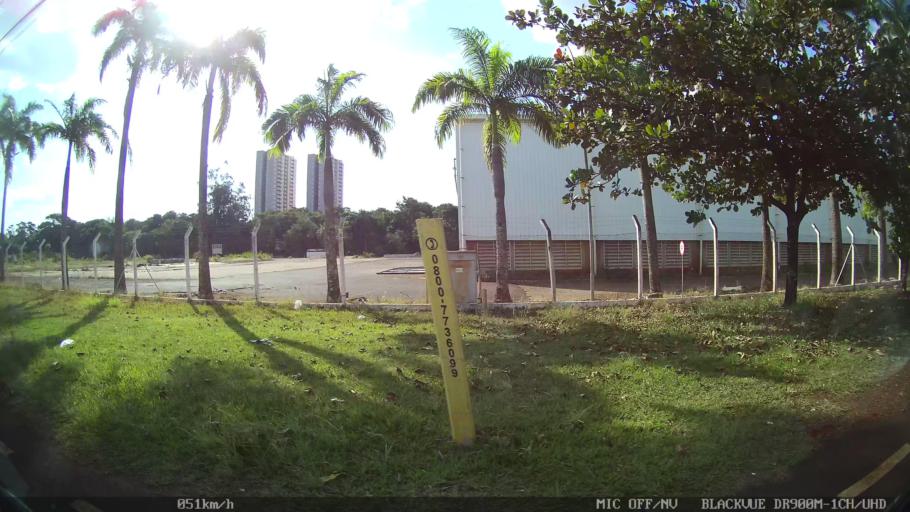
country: BR
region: Sao Paulo
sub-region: Ribeirao Preto
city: Ribeirao Preto
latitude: -21.1779
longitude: -47.8284
